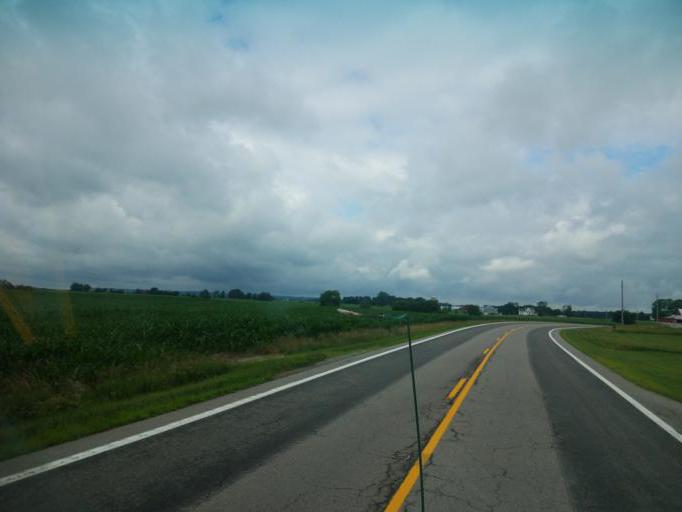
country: US
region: Ohio
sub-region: Champaign County
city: North Lewisburg
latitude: 40.4067
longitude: -83.5578
